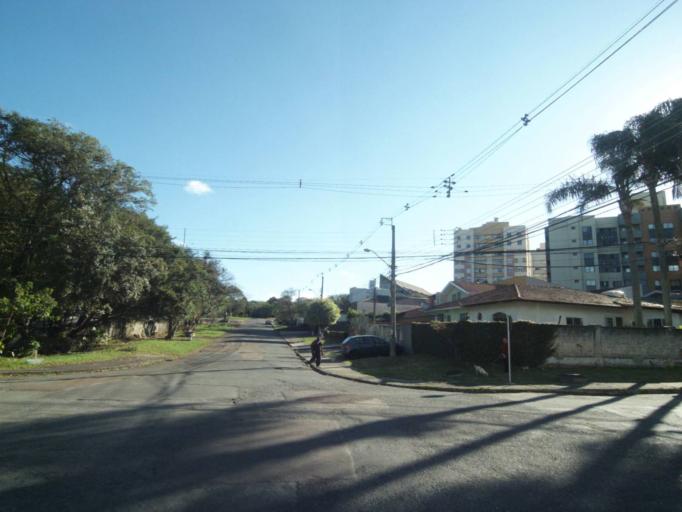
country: BR
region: Parana
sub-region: Curitiba
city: Curitiba
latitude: -25.4005
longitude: -49.2513
